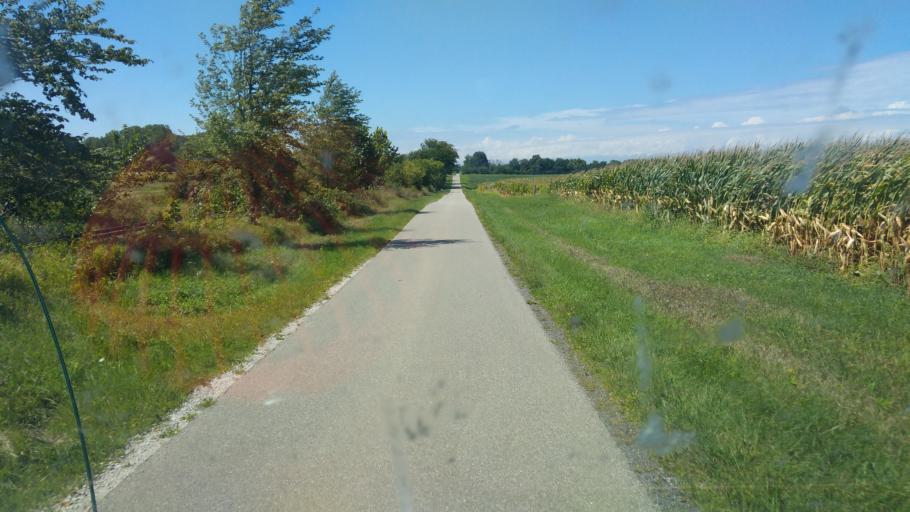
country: US
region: Ohio
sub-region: Crawford County
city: Bucyrus
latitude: 40.8130
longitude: -83.0405
